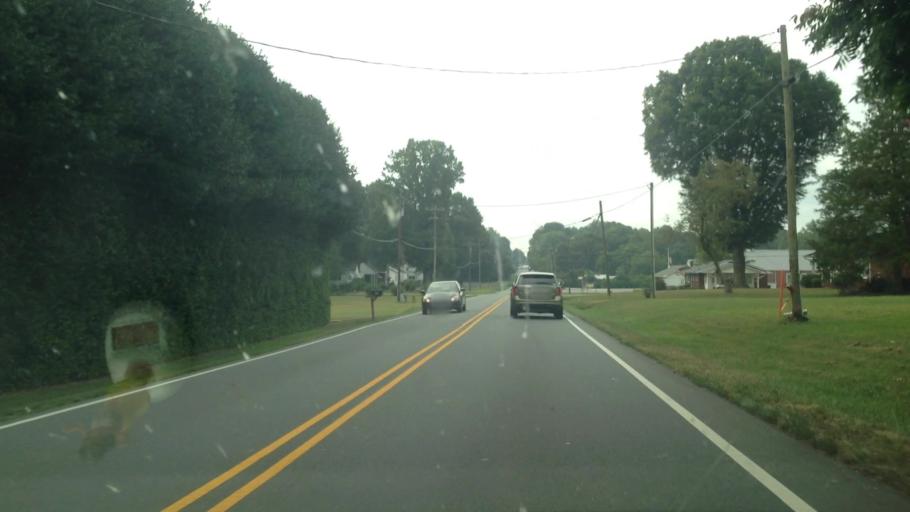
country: US
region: North Carolina
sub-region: Forsyth County
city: Walkertown
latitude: 36.1430
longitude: -80.1265
